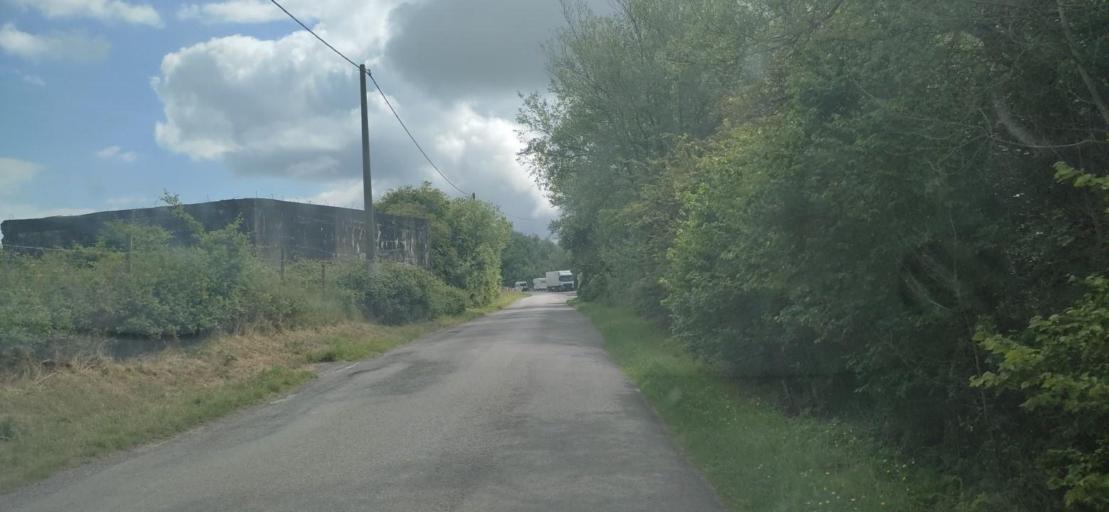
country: FR
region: Nord-Pas-de-Calais
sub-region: Departement du Pas-de-Calais
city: Oye-Plage
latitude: 50.9969
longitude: 2.0529
